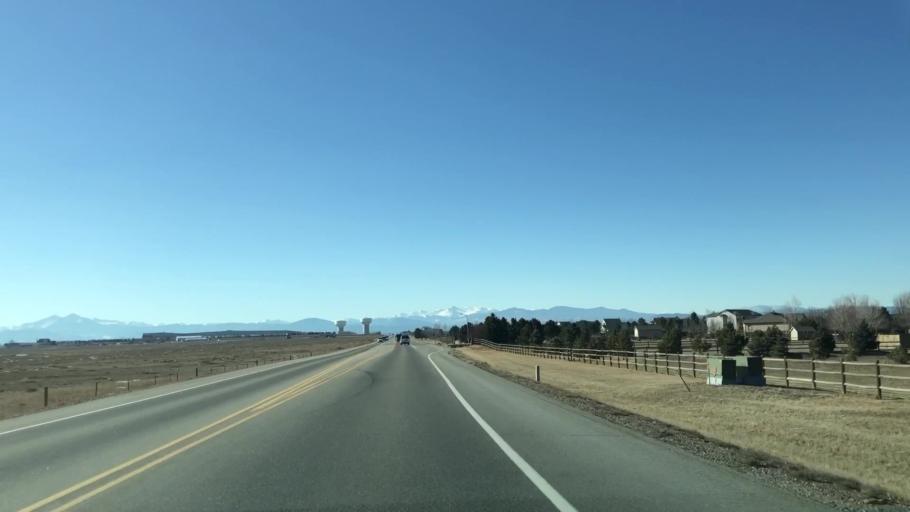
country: US
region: Colorado
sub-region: Weld County
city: Windsor
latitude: 40.4360
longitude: -104.9489
